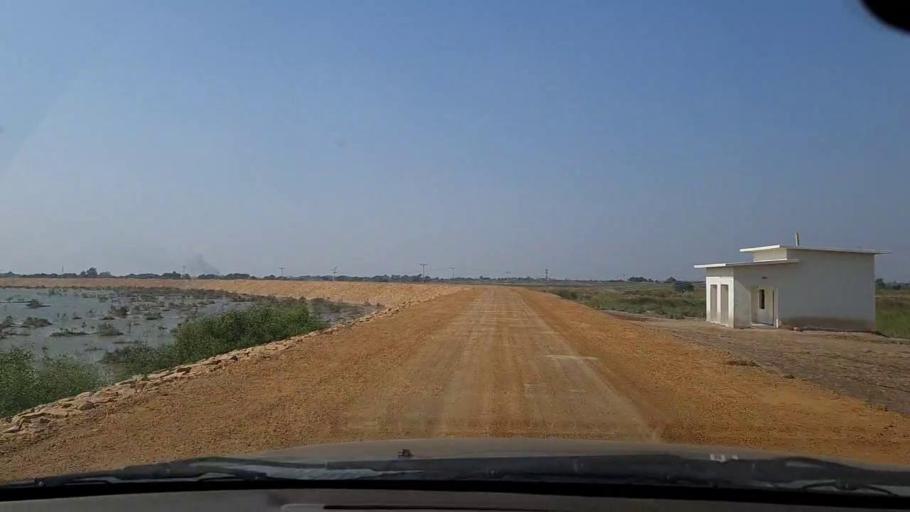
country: PK
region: Sindh
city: Chuhar Jamali
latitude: 24.4566
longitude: 67.8684
